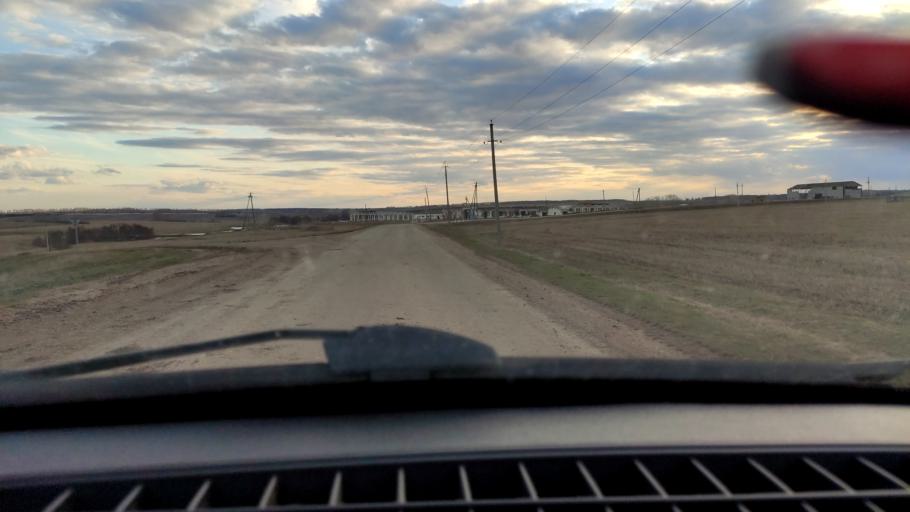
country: RU
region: Bashkortostan
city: Tolbazy
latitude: 53.9960
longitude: 55.6740
